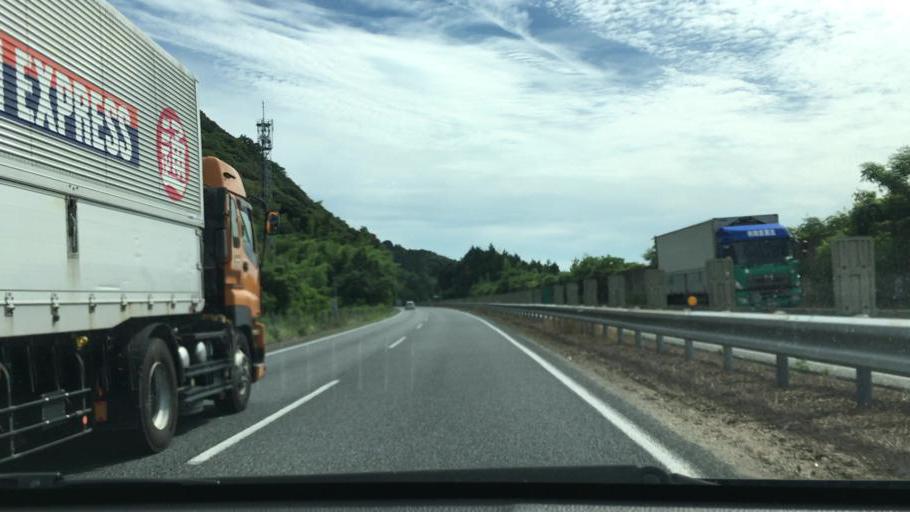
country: JP
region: Yamaguchi
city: Ogori-shimogo
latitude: 34.1289
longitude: 131.4224
